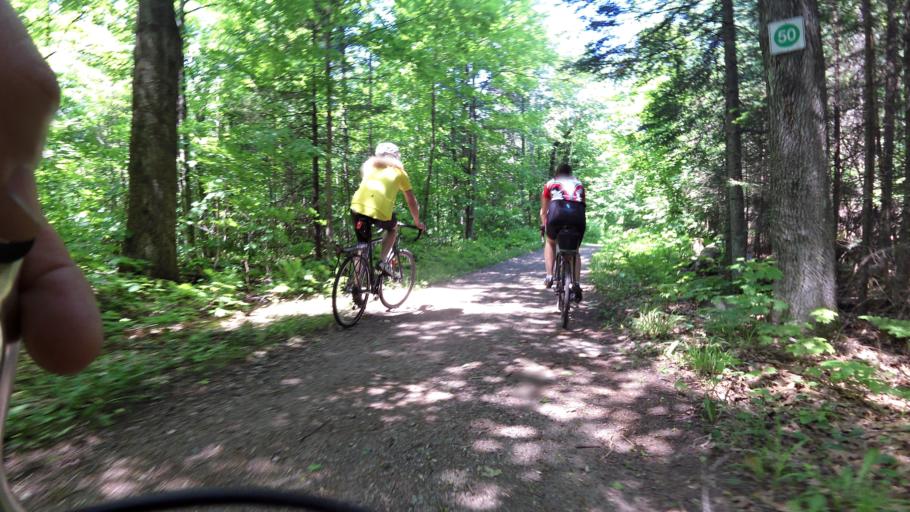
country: CA
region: Quebec
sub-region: Outaouais
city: Wakefield
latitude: 45.5674
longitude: -75.9126
